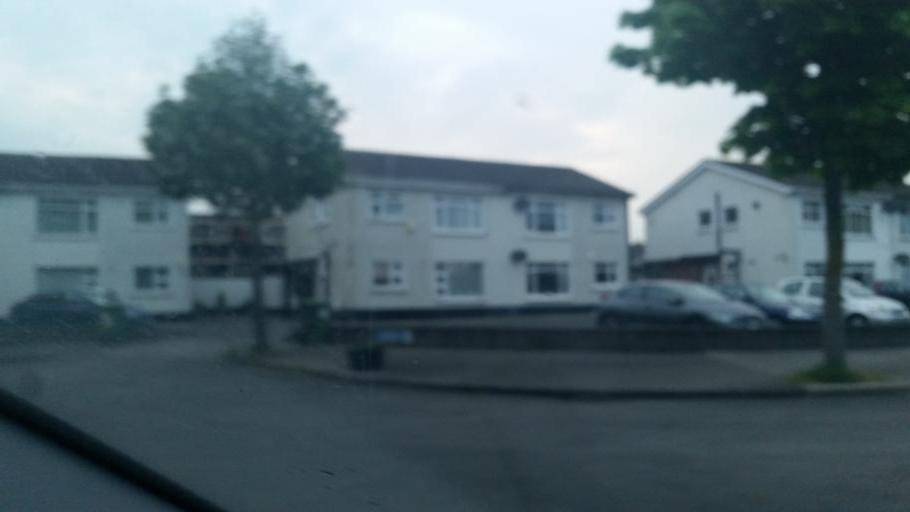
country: IE
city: Darndale
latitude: 53.3916
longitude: -6.1894
